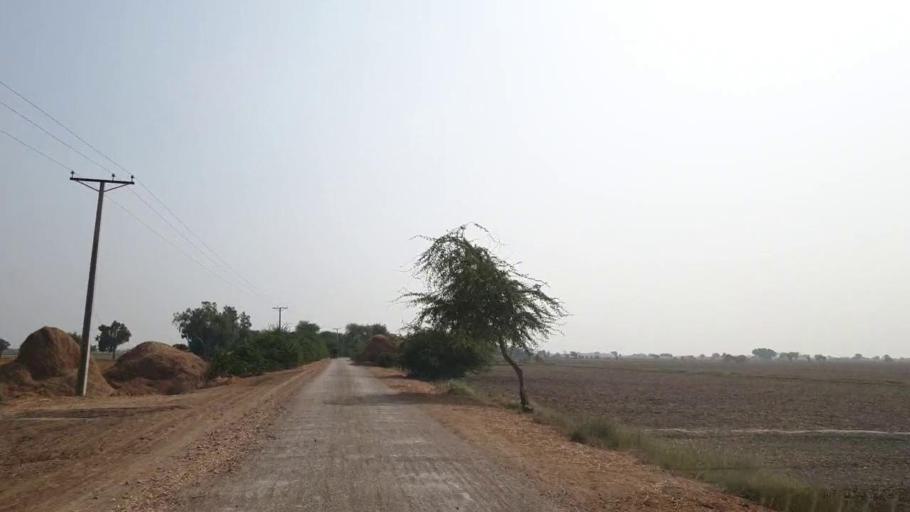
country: PK
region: Sindh
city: Matli
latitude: 24.9963
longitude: 68.5761
